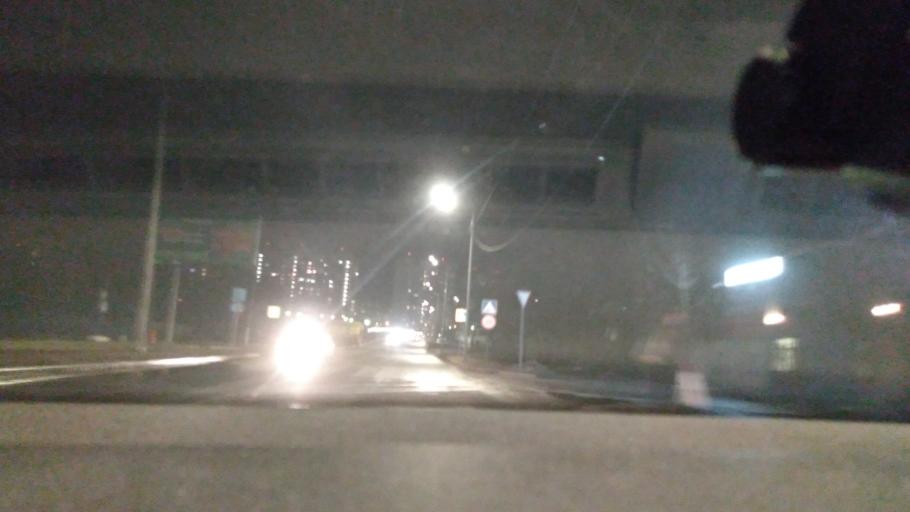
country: RU
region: Moskovskaya
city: Balashikha
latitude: 55.8312
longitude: 37.9498
